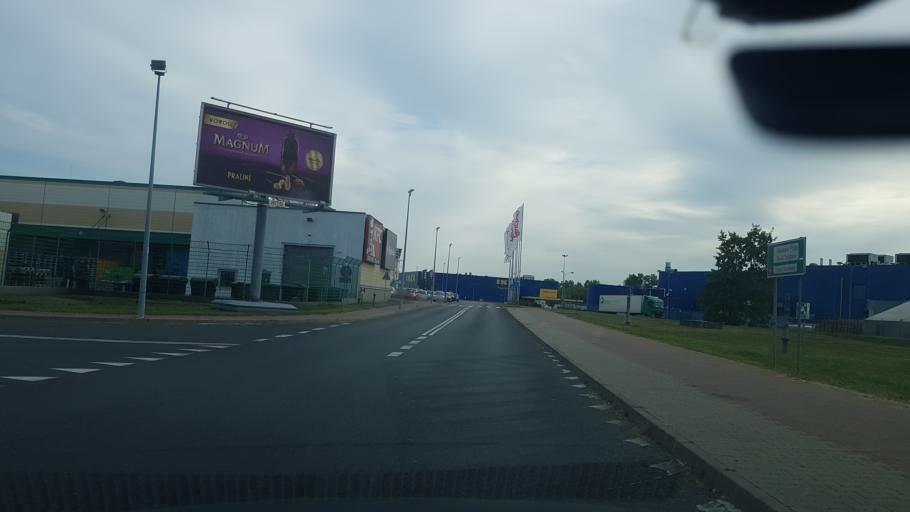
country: PL
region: Masovian Voivodeship
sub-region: Powiat wolominski
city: Marki
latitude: 52.3069
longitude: 21.0847
